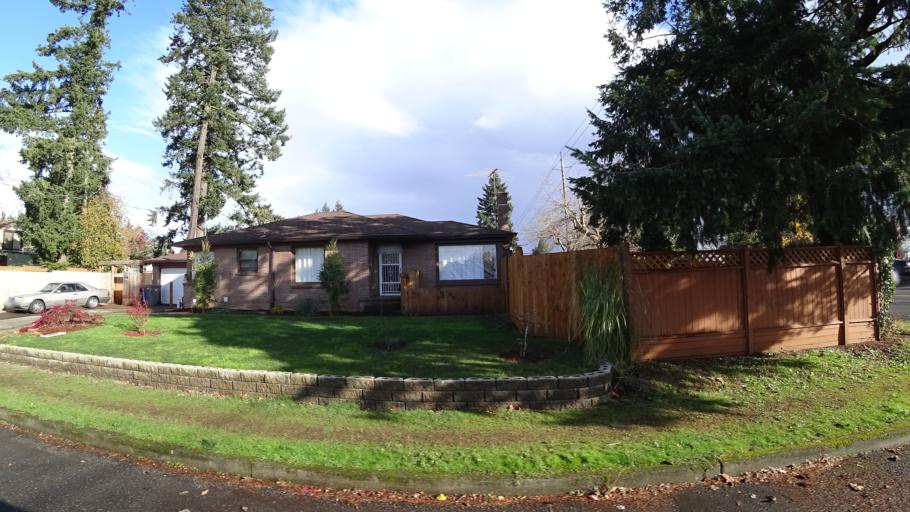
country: US
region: Oregon
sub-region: Multnomah County
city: Lents
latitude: 45.5265
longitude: -122.5448
